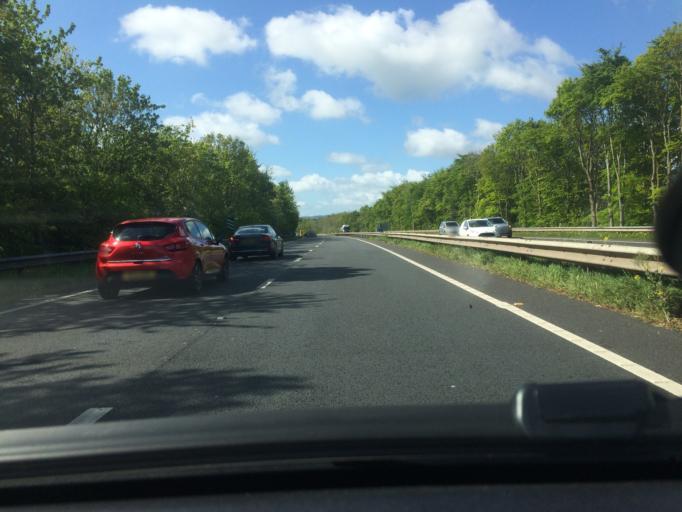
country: GB
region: Wales
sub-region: Wrexham
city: Wrexham
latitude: 53.0621
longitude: -3.0040
